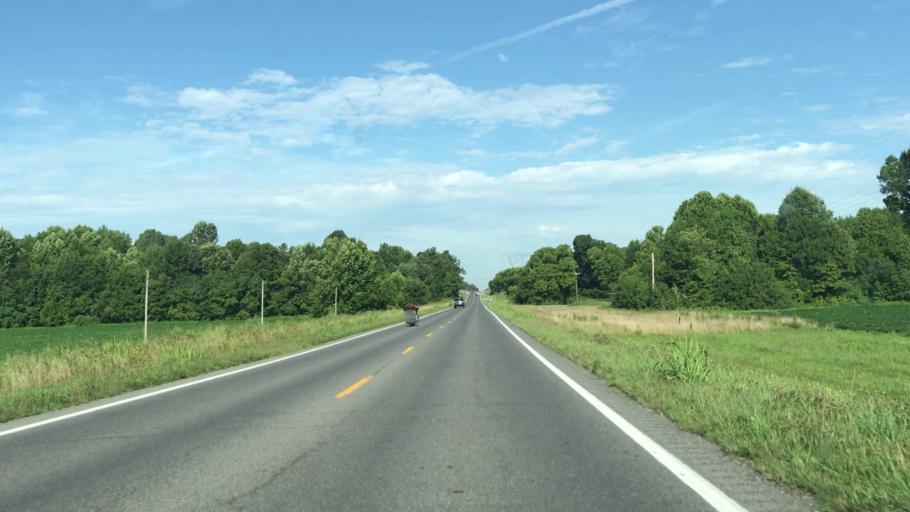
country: US
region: Kentucky
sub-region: Marshall County
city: Calvert City
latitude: 37.0054
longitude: -88.4077
